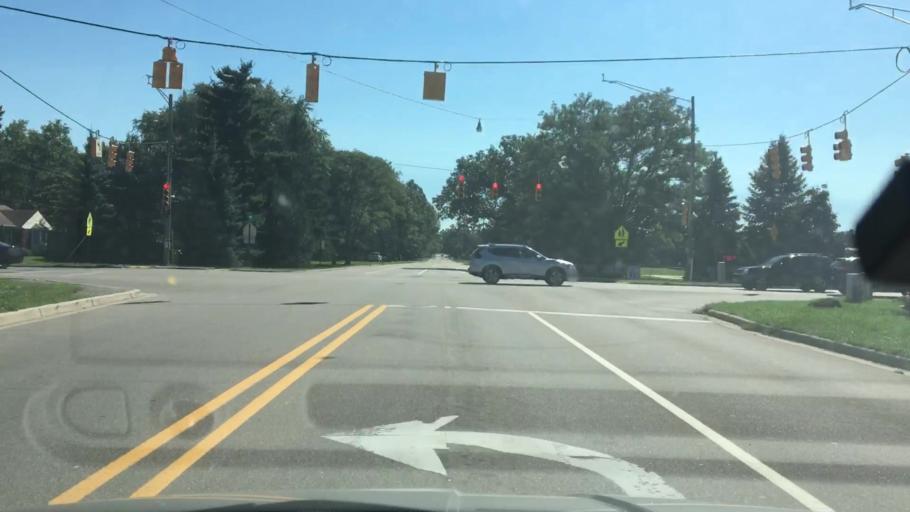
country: US
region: Michigan
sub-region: Livingston County
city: Brighton
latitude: 42.5080
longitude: -83.7689
